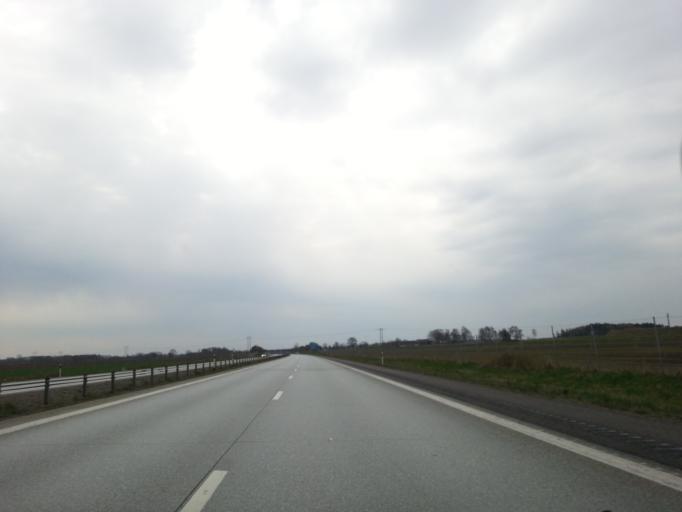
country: SE
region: Halland
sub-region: Falkenbergs Kommun
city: Falkenberg
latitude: 56.9406
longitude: 12.4898
